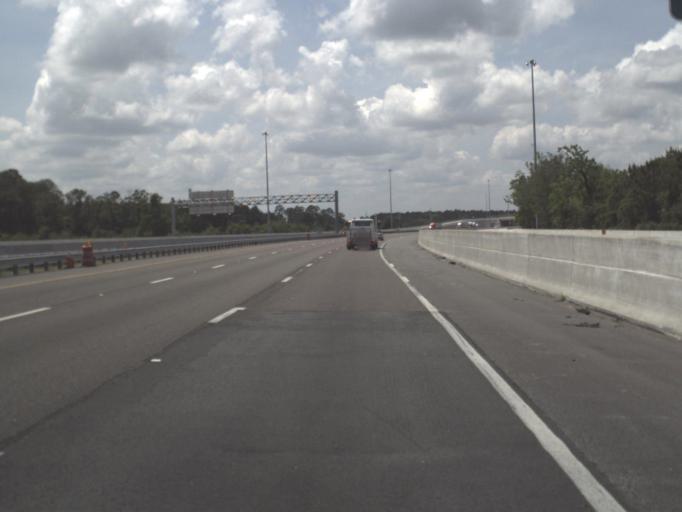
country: US
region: Florida
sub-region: Clay County
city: Bellair-Meadowbrook Terrace
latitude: 30.2004
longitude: -81.7488
